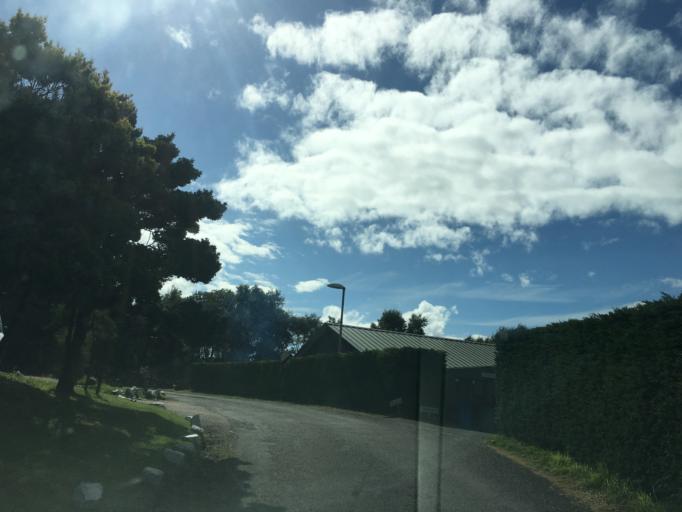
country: GB
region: Scotland
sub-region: Argyll and Bute
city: Oban
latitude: 56.4530
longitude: -5.4038
